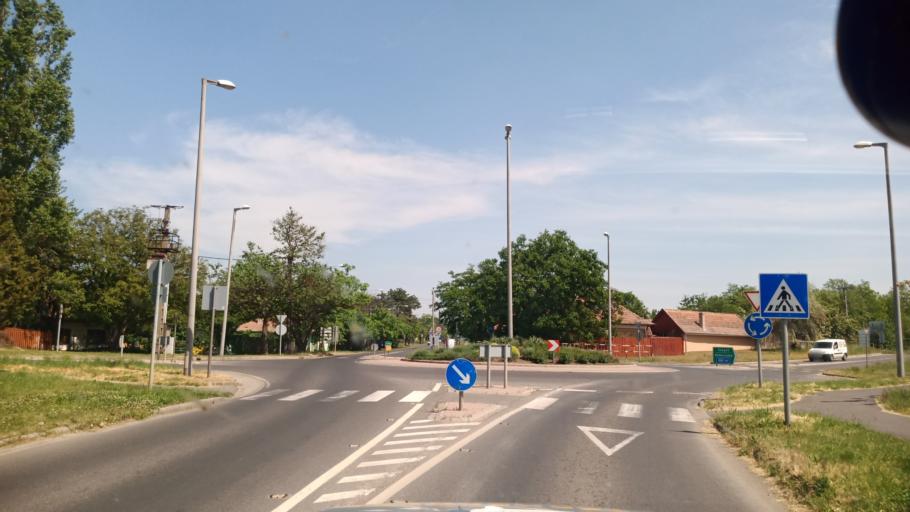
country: HU
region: Bekes
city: Oroshaza
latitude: 46.5600
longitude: 20.6322
